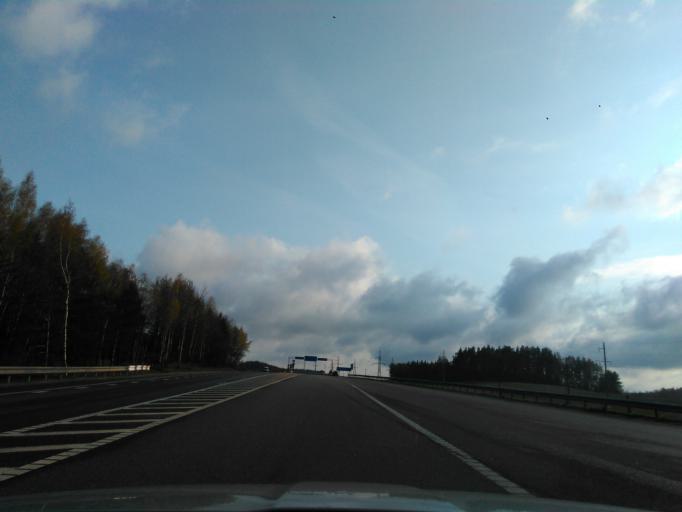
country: BY
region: Minsk
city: Lahoysk
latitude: 54.2123
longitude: 27.8263
